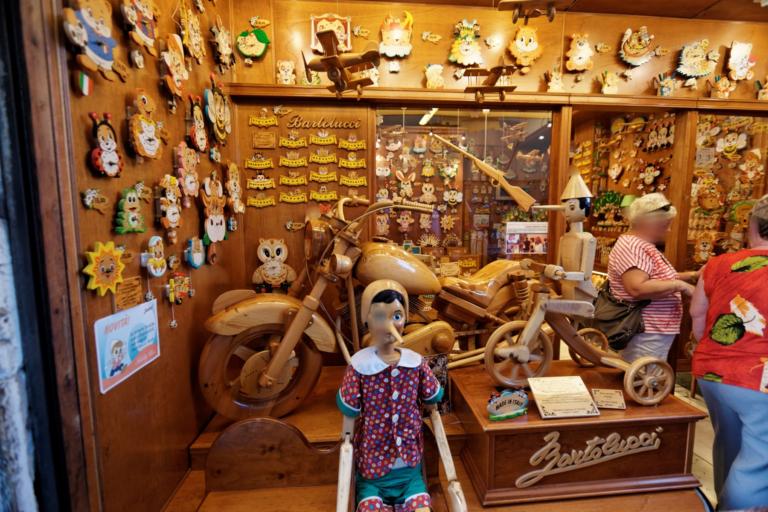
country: IT
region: Veneto
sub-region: Provincia di Venezia
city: Venice
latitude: 45.4378
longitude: 12.3364
